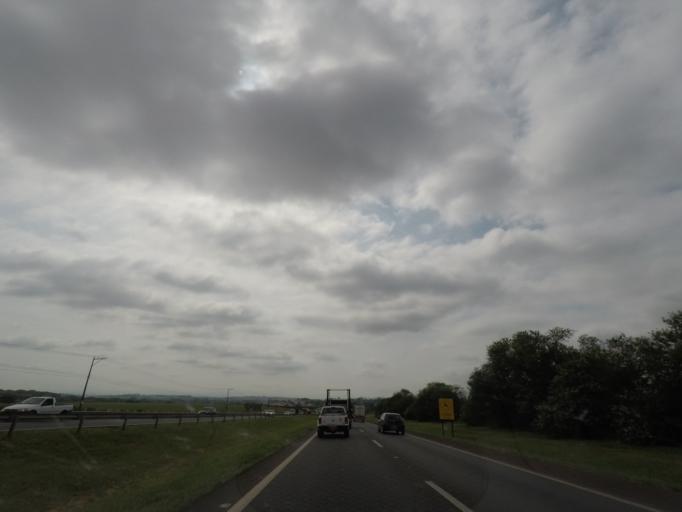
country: BR
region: Sao Paulo
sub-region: Paulinia
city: Paulinia
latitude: -22.8108
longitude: -47.1117
